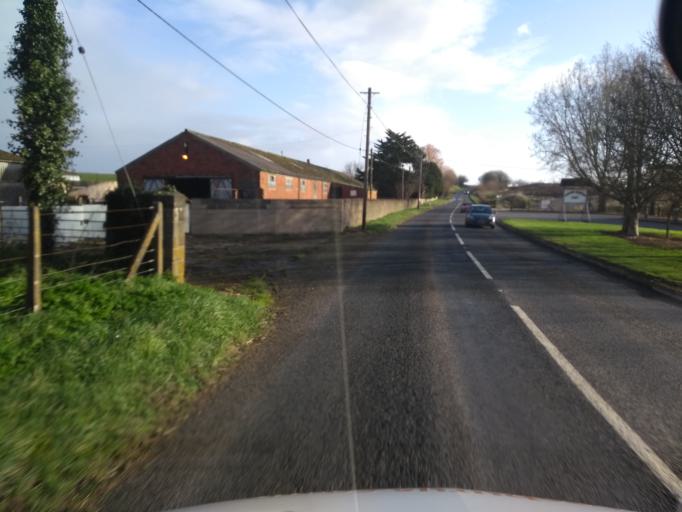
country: GB
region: England
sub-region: Somerset
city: Castle Cary
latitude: 51.0477
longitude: -2.5458
